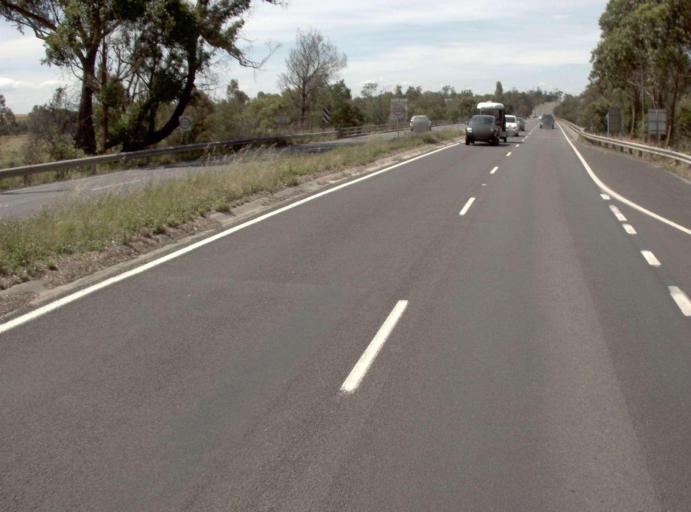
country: AU
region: Victoria
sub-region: Wellington
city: Heyfield
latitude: -38.1488
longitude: 146.7903
